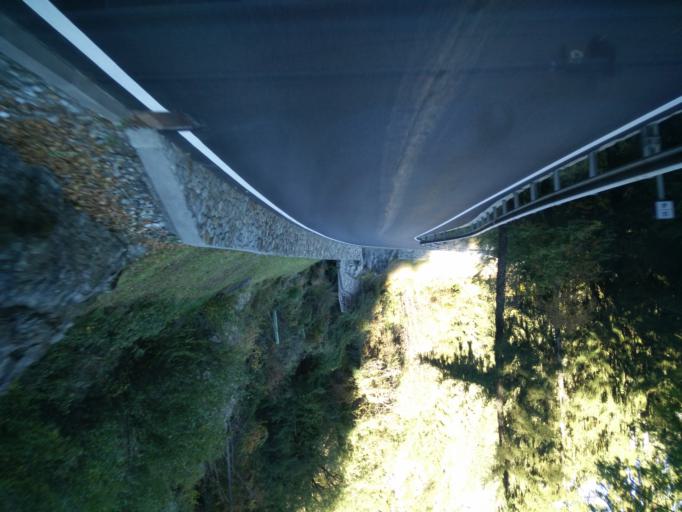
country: IT
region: Trentino-Alto Adige
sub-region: Bolzano
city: Moso in Passiria
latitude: 46.8239
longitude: 11.1939
